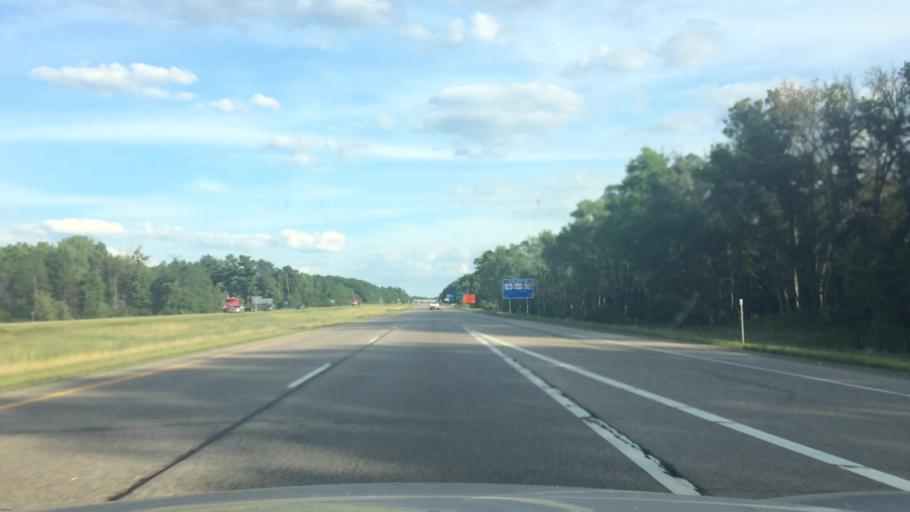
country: US
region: Wisconsin
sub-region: Portage County
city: Stevens Point
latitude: 44.5680
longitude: -89.5968
